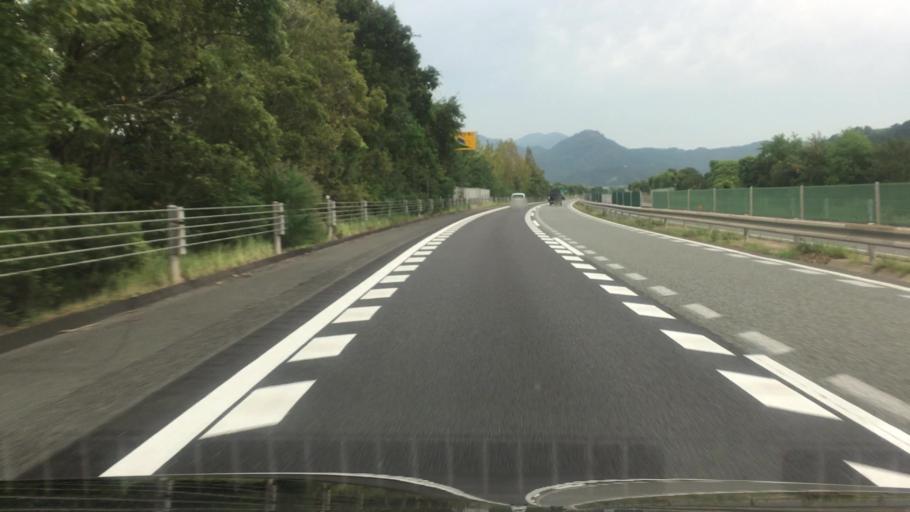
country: JP
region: Hyogo
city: Sasayama
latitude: 35.1430
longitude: 135.1277
